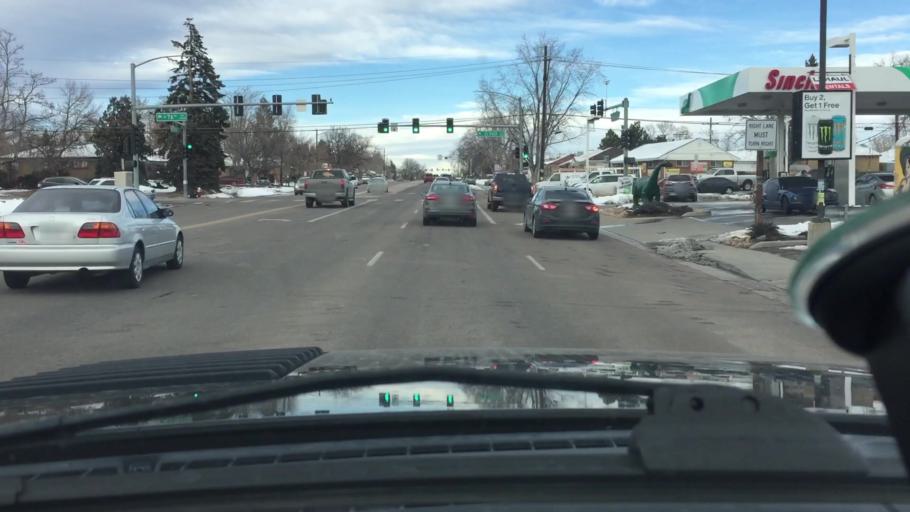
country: US
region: Colorado
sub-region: Adams County
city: Sherrelwood
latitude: 39.8339
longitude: -105.0061
